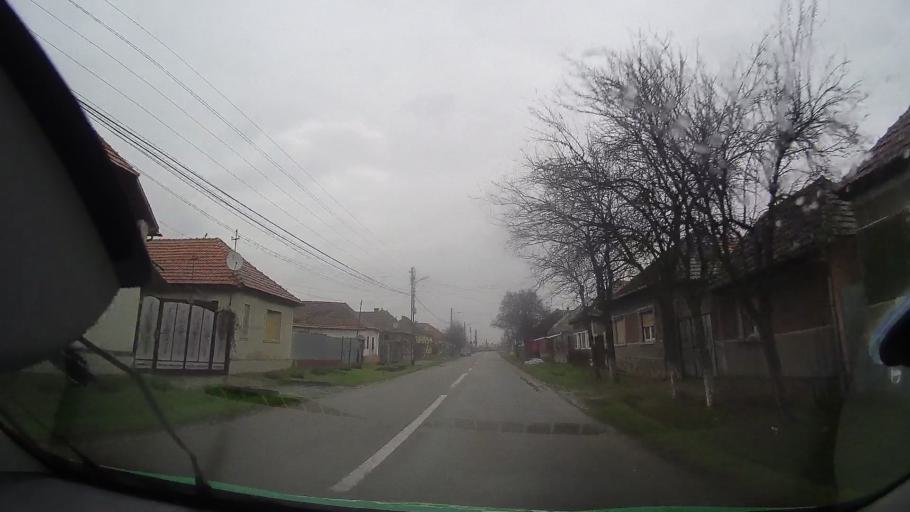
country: RO
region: Bihor
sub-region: Comuna Tinca
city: Tinca
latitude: 46.7389
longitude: 21.9452
